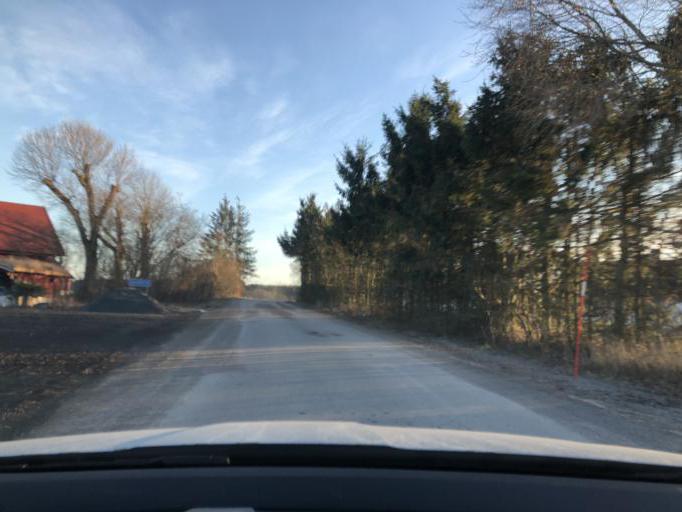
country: SE
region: Soedermanland
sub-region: Eskilstuna Kommun
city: Arla
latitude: 59.4347
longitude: 16.6579
